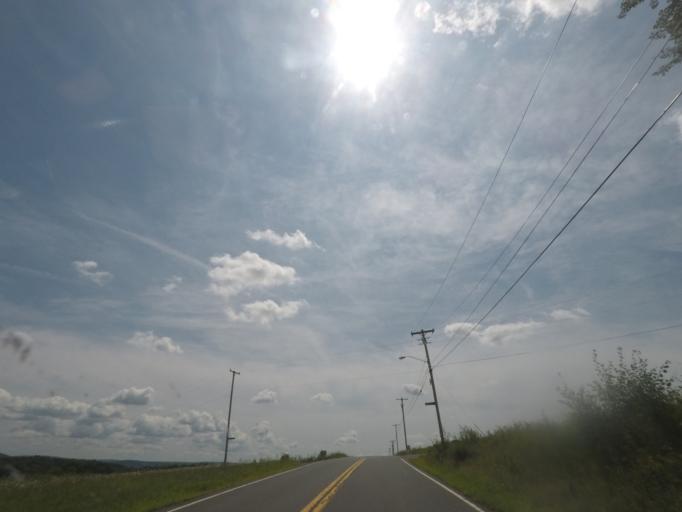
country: US
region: New York
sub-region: Rensselaer County
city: Wynantskill
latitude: 42.7129
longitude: -73.6085
